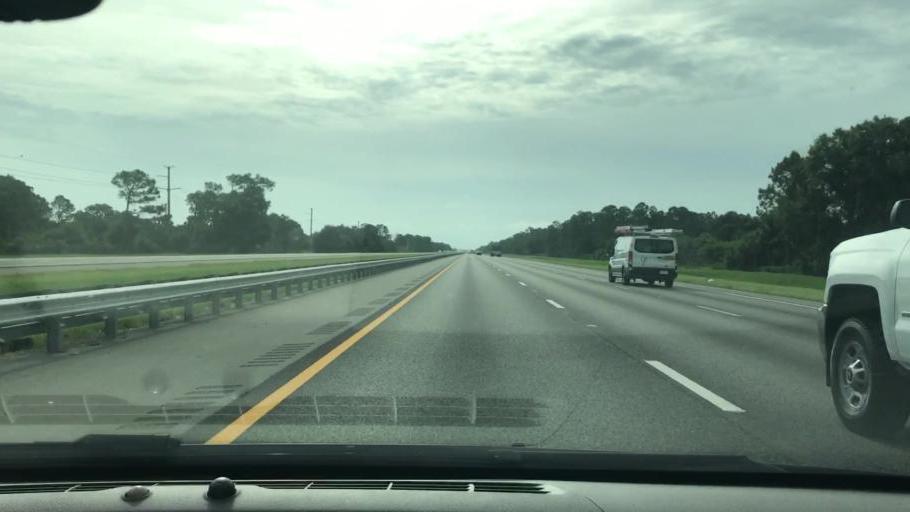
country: US
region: Florida
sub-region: Charlotte County
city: Port Charlotte
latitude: 27.0765
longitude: -82.1039
